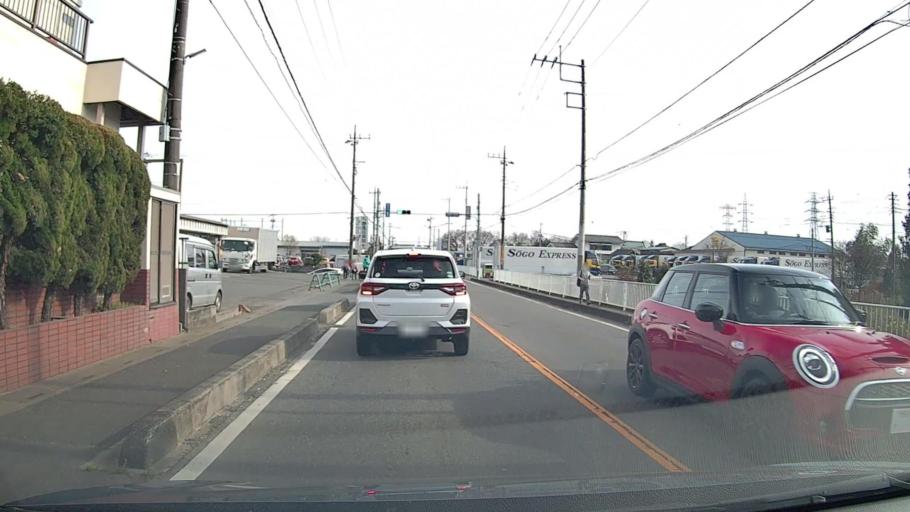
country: JP
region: Saitama
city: Asaka
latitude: 35.7784
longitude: 139.5604
